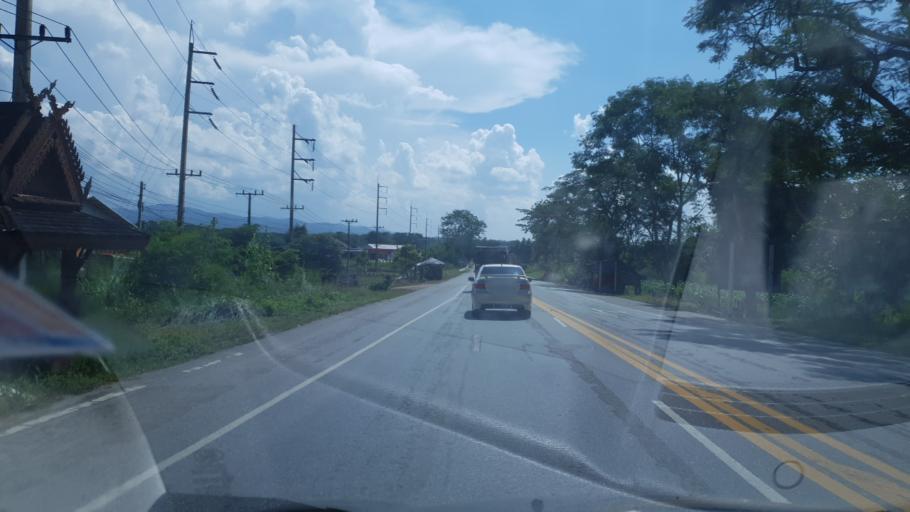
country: TH
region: Chiang Rai
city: Mae Suai
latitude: 19.6722
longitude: 99.5530
